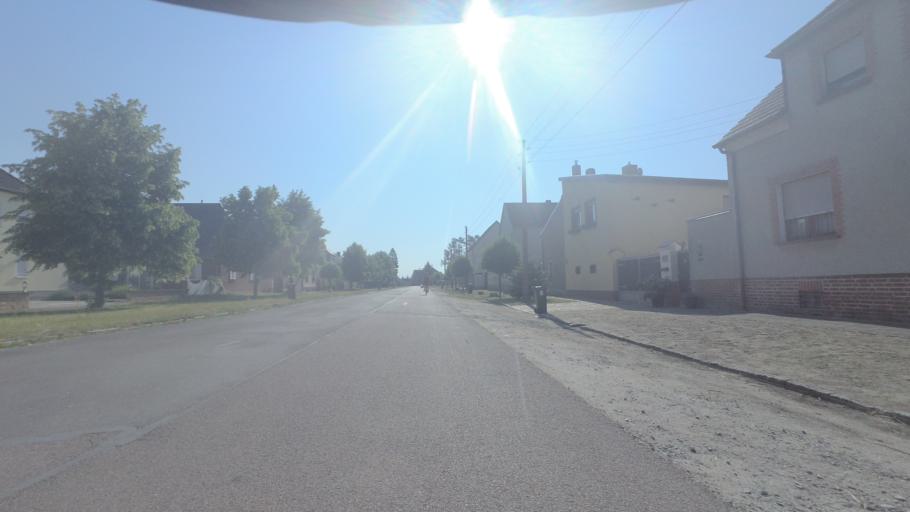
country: DE
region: Saxony-Anhalt
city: Quellendorf
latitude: 51.8155
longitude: 12.1205
